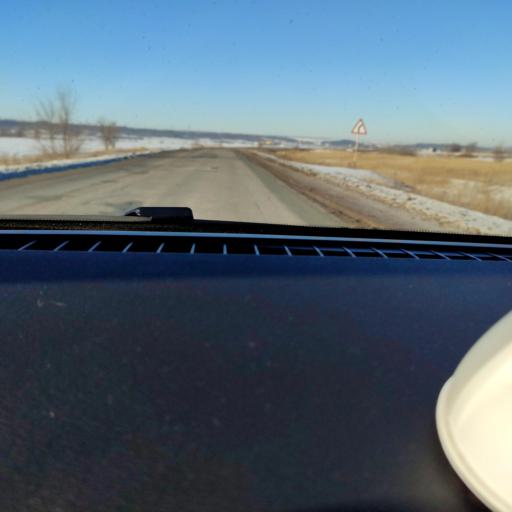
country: RU
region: Samara
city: Spiridonovka
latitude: 53.1259
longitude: 50.6213
